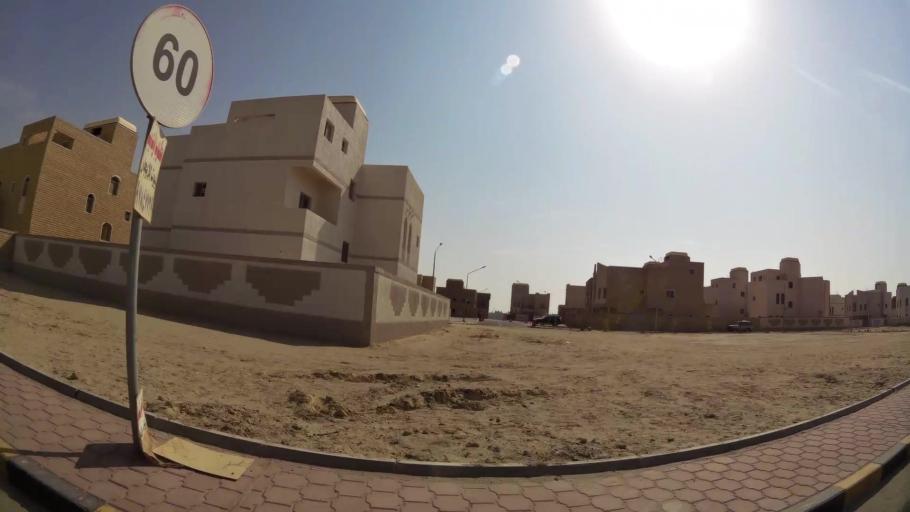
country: KW
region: Al Ahmadi
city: Al Wafrah
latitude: 28.7955
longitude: 48.0759
